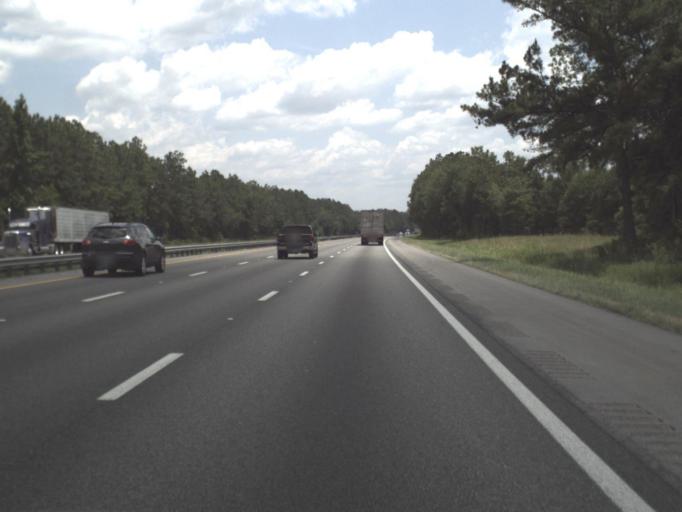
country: US
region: Florida
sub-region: Hamilton County
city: Jasper
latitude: 30.5659
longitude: -83.0918
